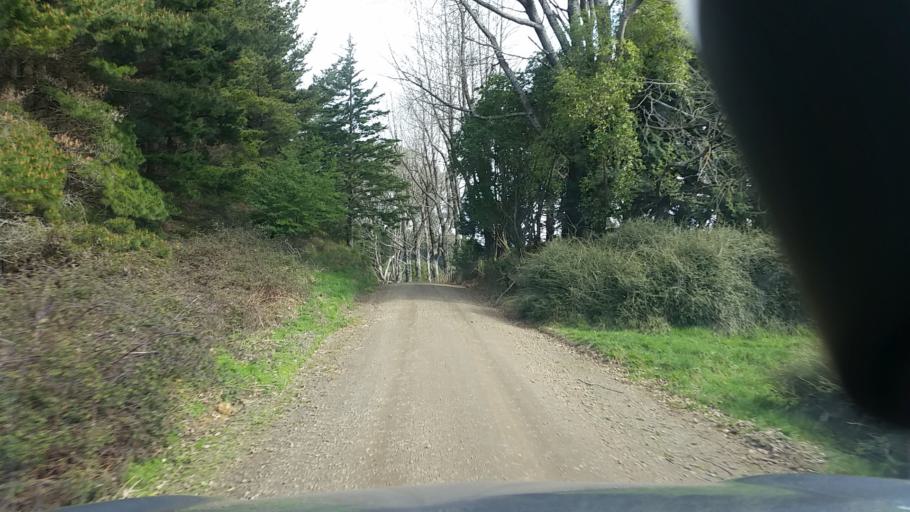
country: NZ
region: Hawke's Bay
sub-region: Napier City
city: Napier
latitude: -39.2275
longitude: 176.9981
